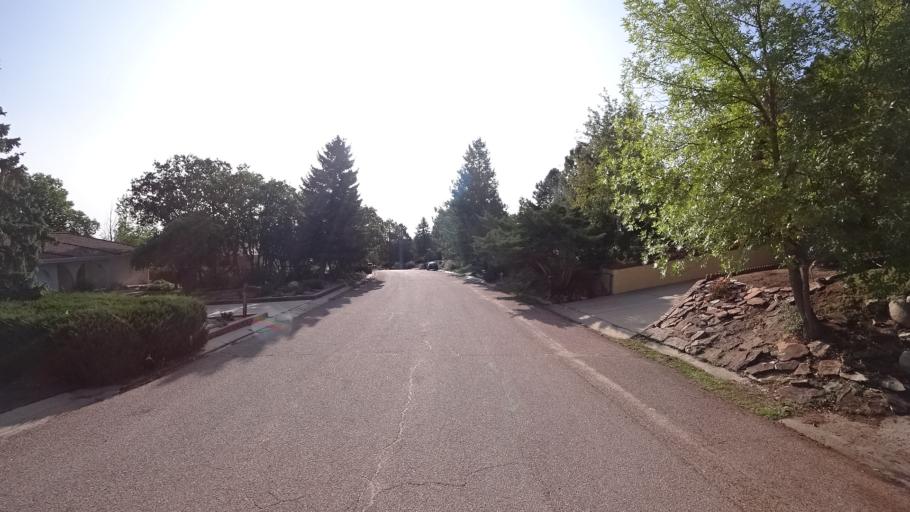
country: US
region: Colorado
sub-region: El Paso County
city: Colorado Springs
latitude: 38.8187
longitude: -104.8664
